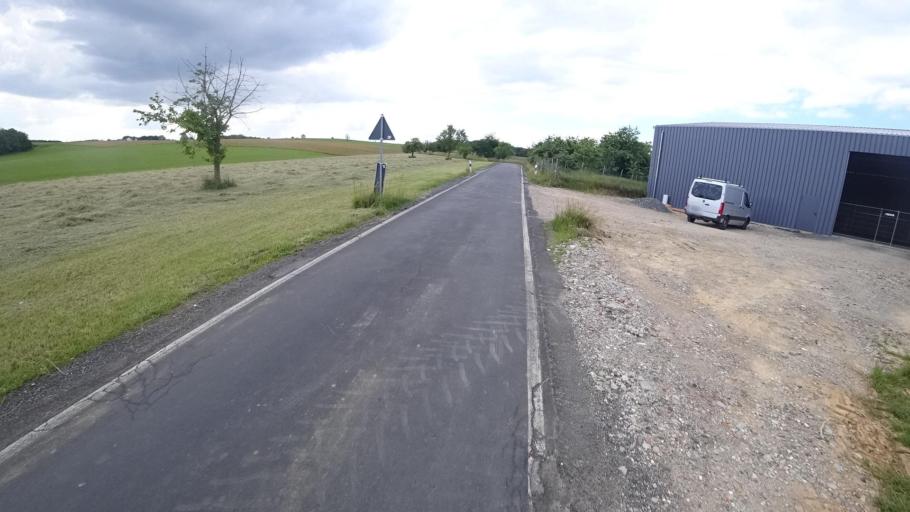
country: DE
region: Rheinland-Pfalz
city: Bachenberg
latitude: 50.7168
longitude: 7.6584
